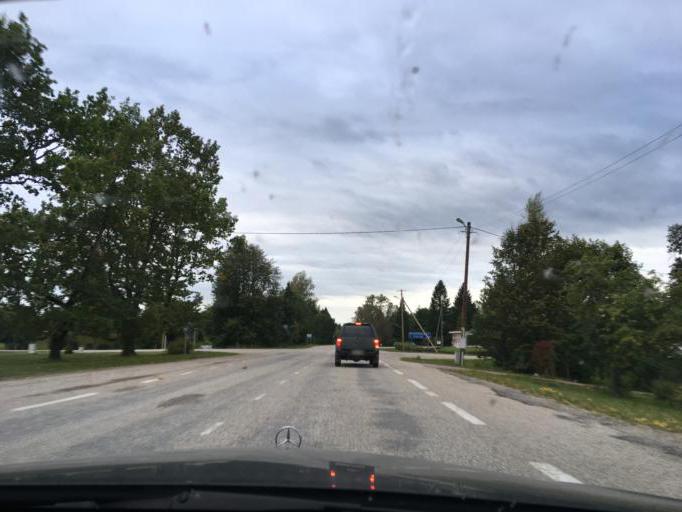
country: LV
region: Aluksnes Rajons
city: Aluksne
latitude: 57.6010
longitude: 27.2294
